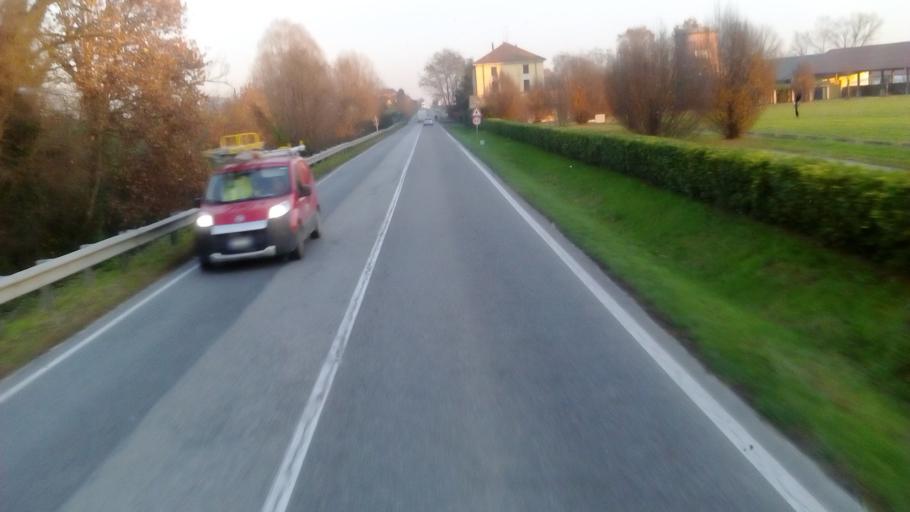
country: IT
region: Lombardy
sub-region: Provincia di Cremona
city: Ticengo
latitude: 45.3731
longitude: 9.8097
